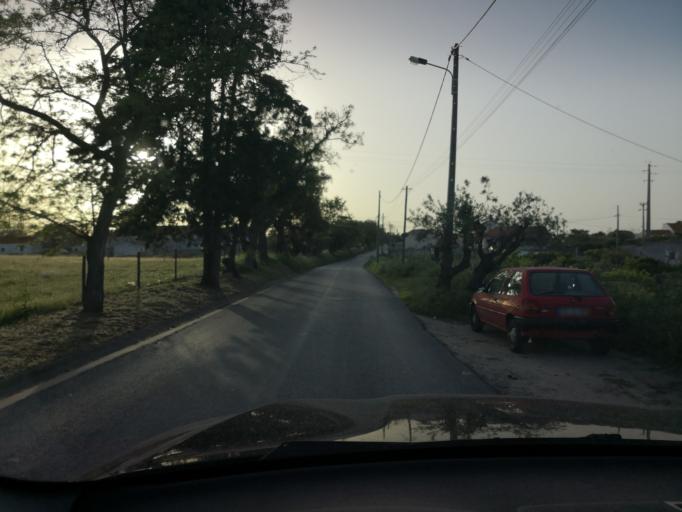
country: PT
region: Setubal
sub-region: Setubal
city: Setubal
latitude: 38.5308
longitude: -8.8109
